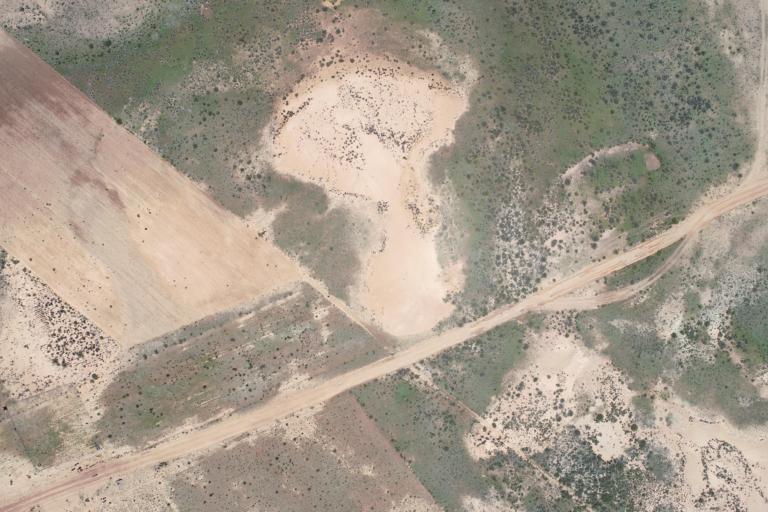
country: BO
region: La Paz
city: Patacamaya
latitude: -17.2854
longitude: -68.5048
